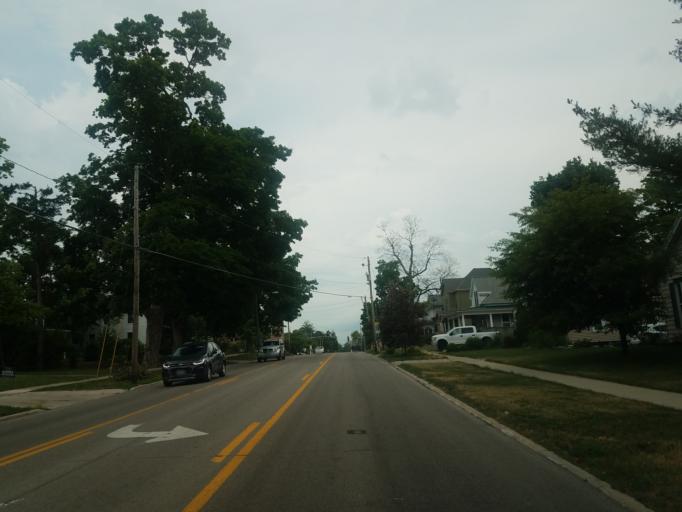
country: US
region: Illinois
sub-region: McLean County
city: Bloomington
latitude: 40.4800
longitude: -88.9731
